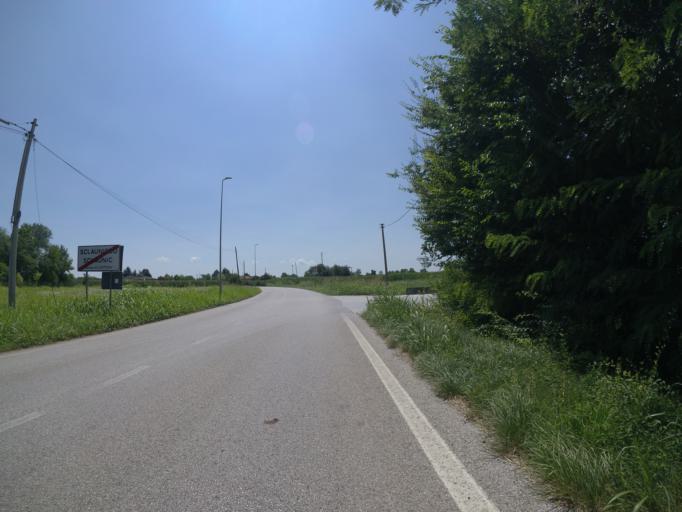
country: IT
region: Friuli Venezia Giulia
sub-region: Provincia di Udine
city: Lestizza
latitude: 45.9716
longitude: 13.1395
